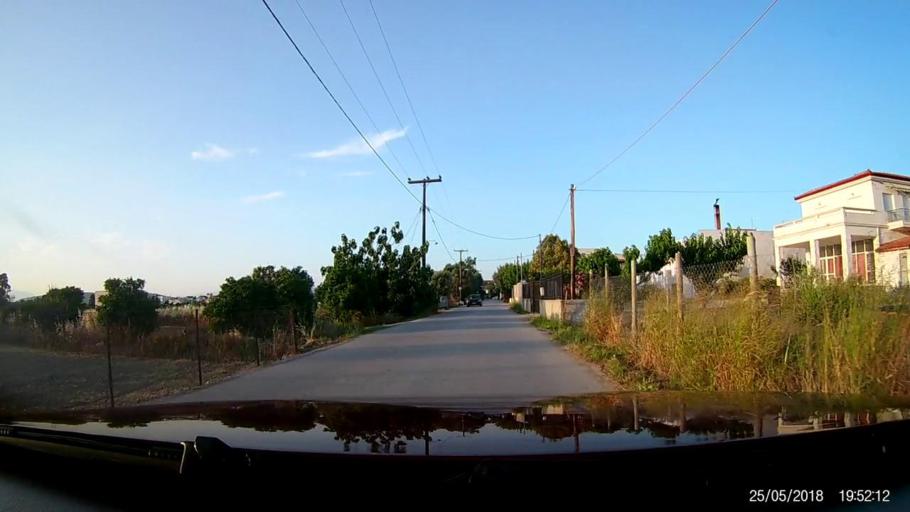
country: GR
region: Central Greece
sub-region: Nomos Evvoias
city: Ayios Nikolaos
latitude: 38.4095
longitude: 23.6441
